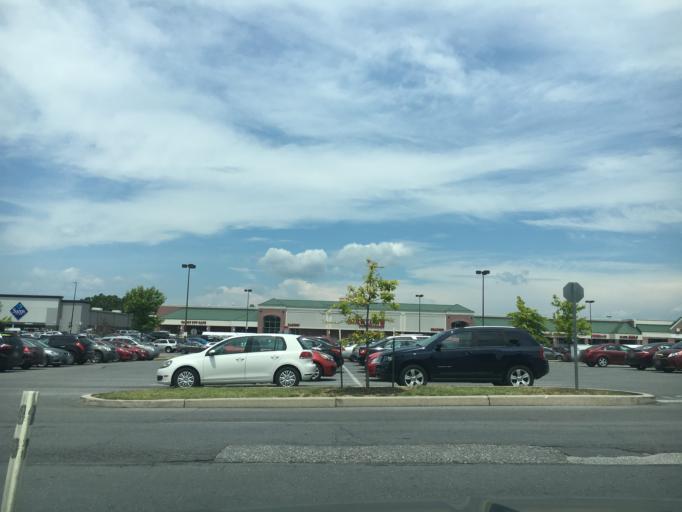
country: US
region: Maryland
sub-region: Washington County
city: Halfway
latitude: 39.6313
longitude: -77.7630
